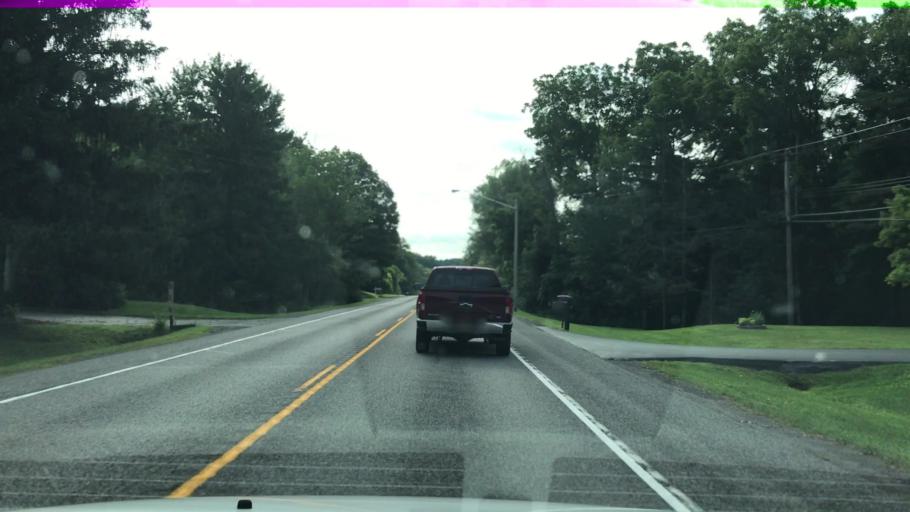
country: US
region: New York
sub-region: Erie County
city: Alden
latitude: 42.8478
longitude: -78.4792
